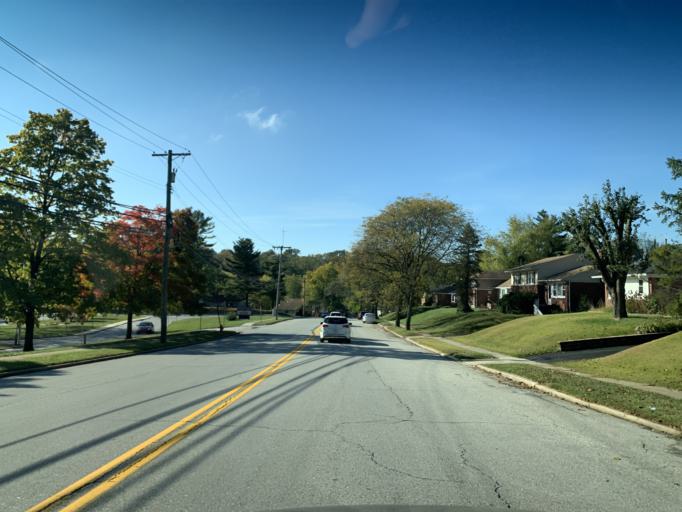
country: US
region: Maryland
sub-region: Baltimore County
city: Hampton
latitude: 39.4047
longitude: -76.5821
